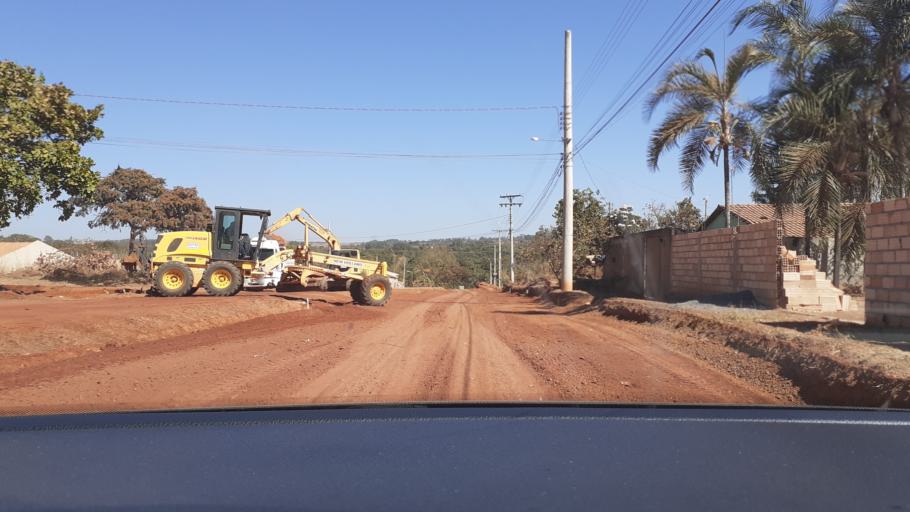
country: BR
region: Goias
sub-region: Aparecida De Goiania
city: Aparecida de Goiania
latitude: -16.8777
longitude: -49.2600
